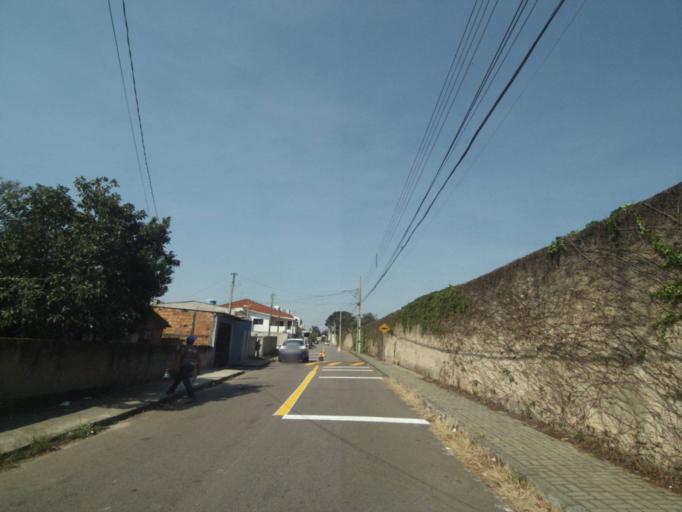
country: BR
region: Parana
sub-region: Curitiba
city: Curitiba
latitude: -25.4827
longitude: -49.3003
